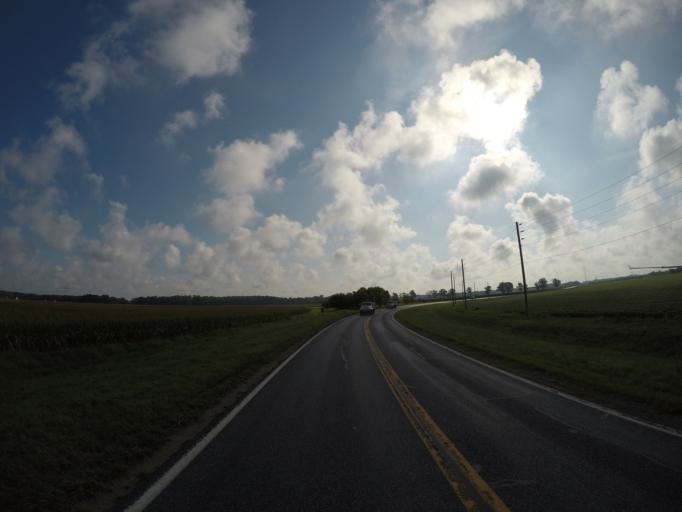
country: US
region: Delaware
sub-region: Sussex County
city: Bridgeville
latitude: 38.7632
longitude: -75.6139
